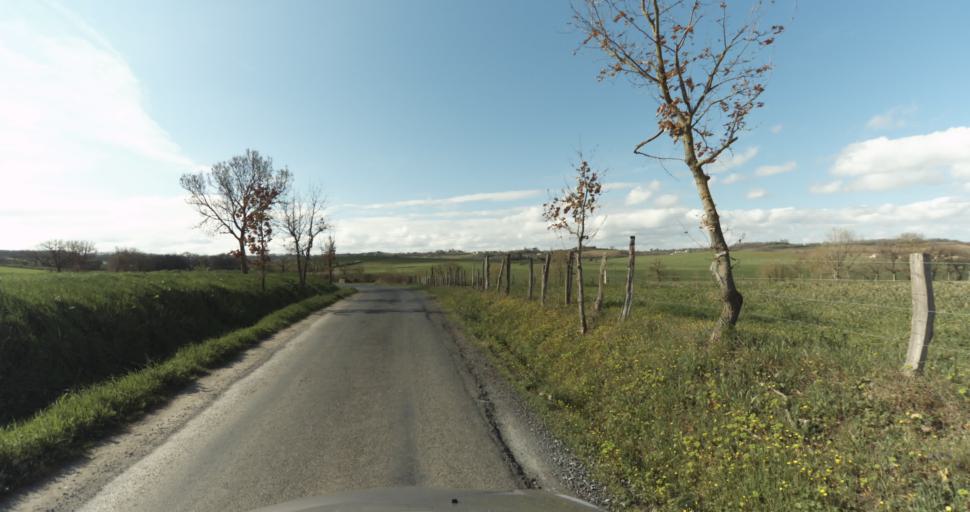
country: FR
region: Midi-Pyrenees
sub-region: Departement du Tarn
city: Puygouzon
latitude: 43.8858
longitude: 2.1826
